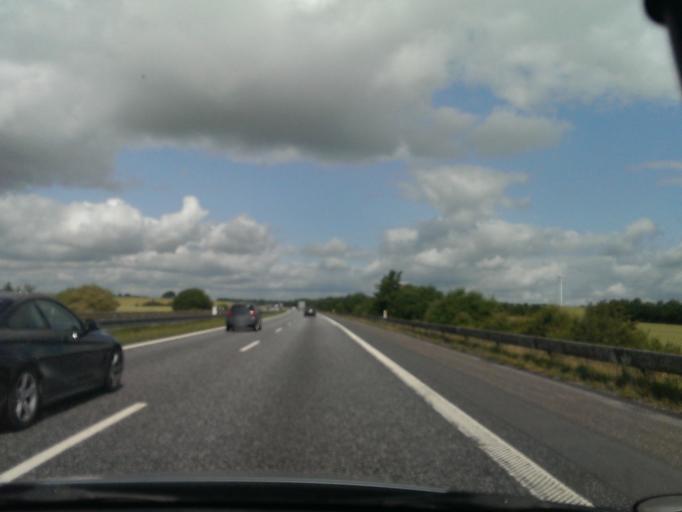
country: DK
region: Central Jutland
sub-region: Randers Kommune
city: Spentrup
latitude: 56.5157
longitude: 9.9636
